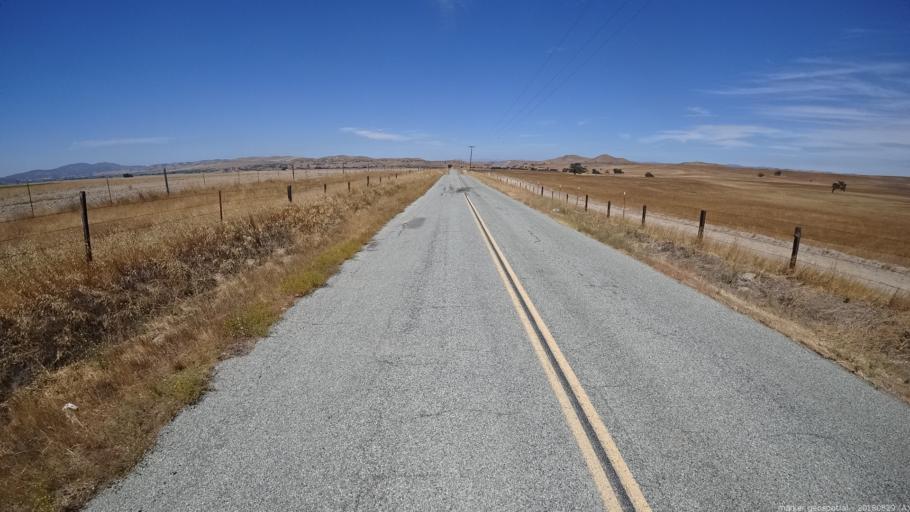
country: US
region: California
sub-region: San Luis Obispo County
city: Lake Nacimiento
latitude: 35.8436
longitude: -120.8417
